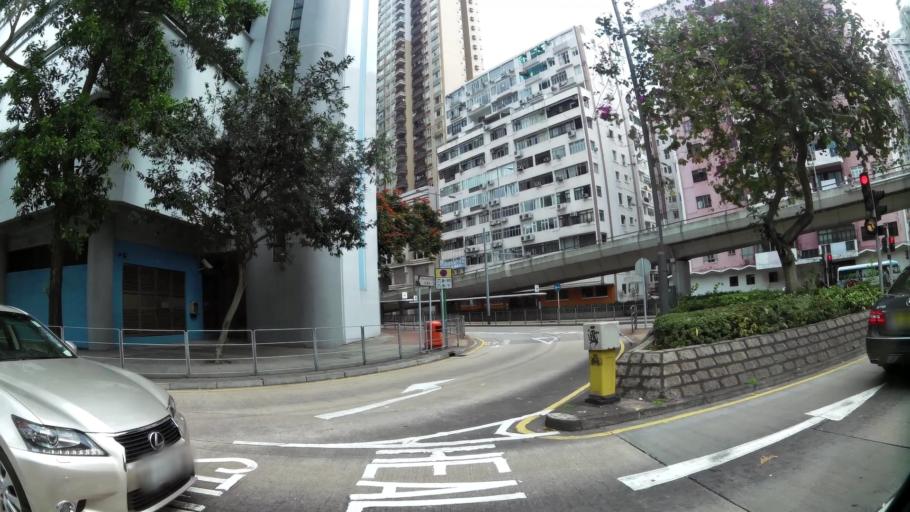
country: HK
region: Kowloon City
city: Kowloon
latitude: 22.2925
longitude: 114.2048
